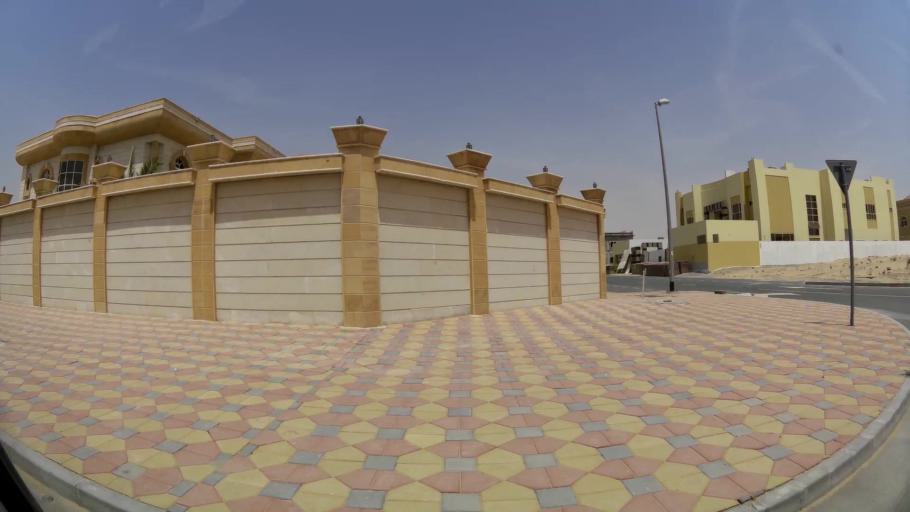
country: AE
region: Ash Shariqah
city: Sharjah
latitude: 25.2480
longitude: 55.5052
